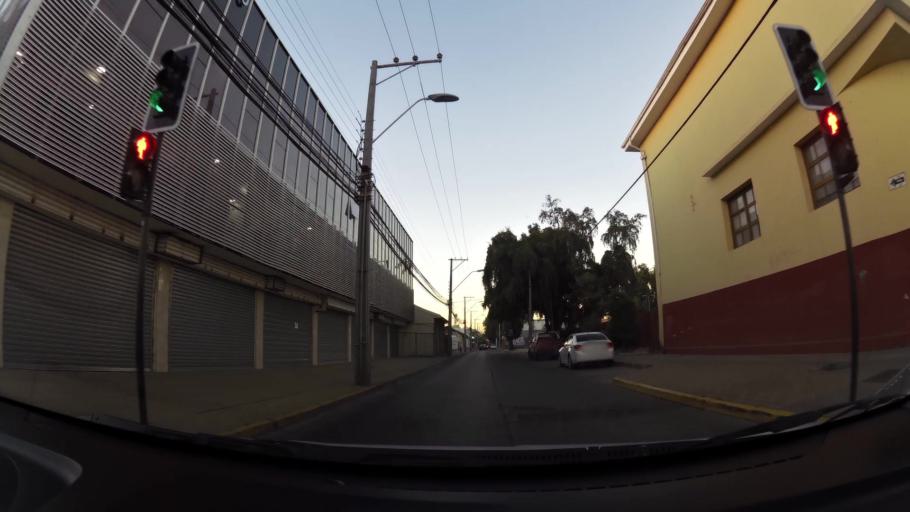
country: CL
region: Maule
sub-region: Provincia de Curico
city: Curico
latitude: -34.9883
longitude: -71.2411
